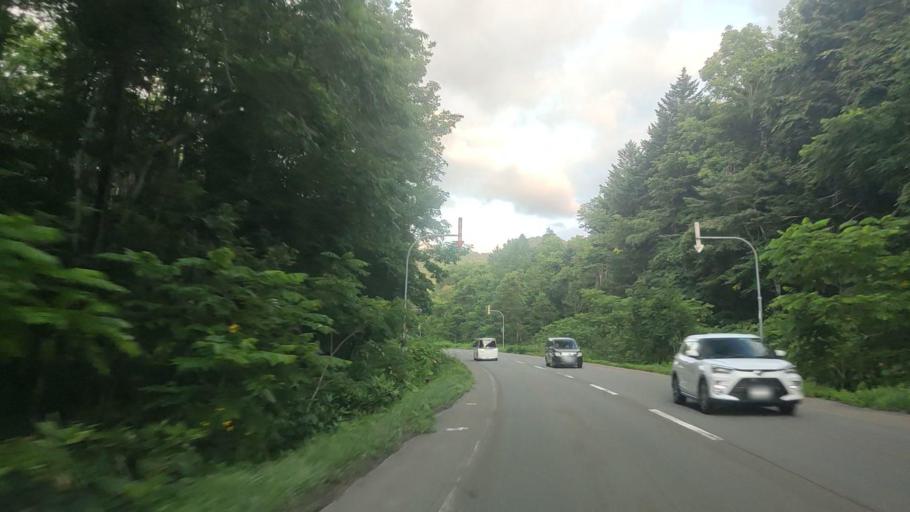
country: JP
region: Hokkaido
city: Ashibetsu
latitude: 43.3763
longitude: 142.1949
